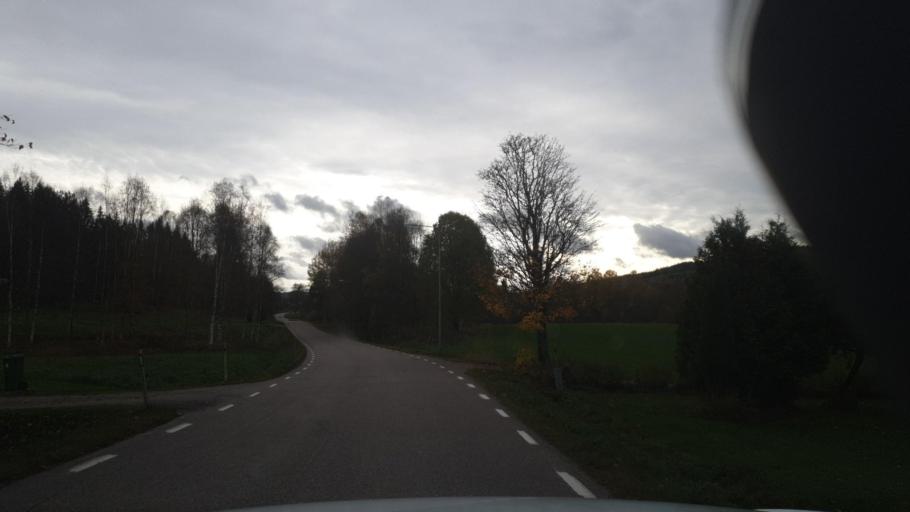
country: SE
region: Vaermland
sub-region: Arvika Kommun
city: Arvika
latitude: 59.7611
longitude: 12.7945
